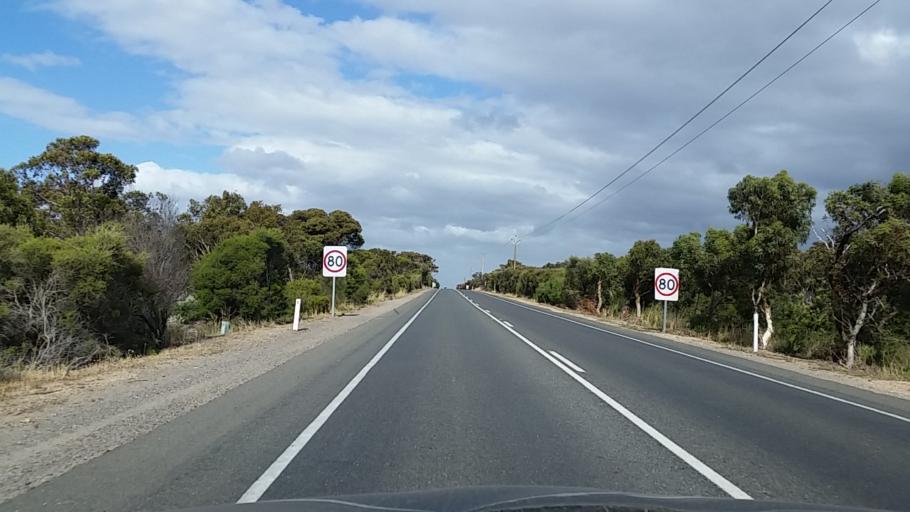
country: AU
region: South Australia
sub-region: Alexandrina
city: Goolwa
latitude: -35.5058
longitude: 138.7636
